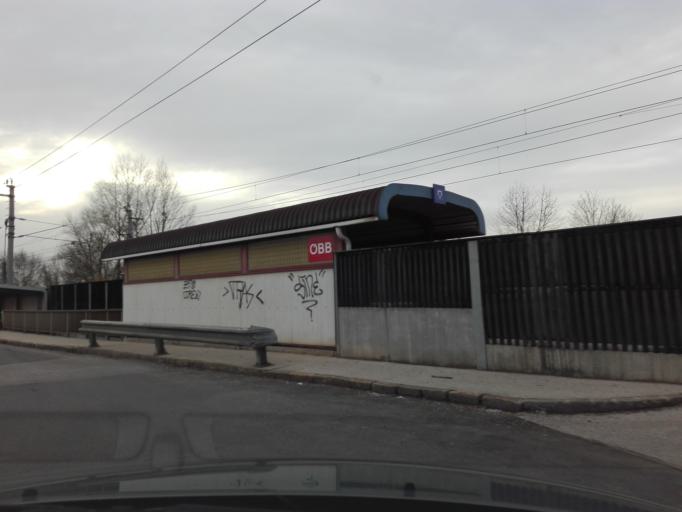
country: AT
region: Upper Austria
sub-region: Politischer Bezirk Linz-Land
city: Horsching
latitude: 48.2274
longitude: 14.1515
